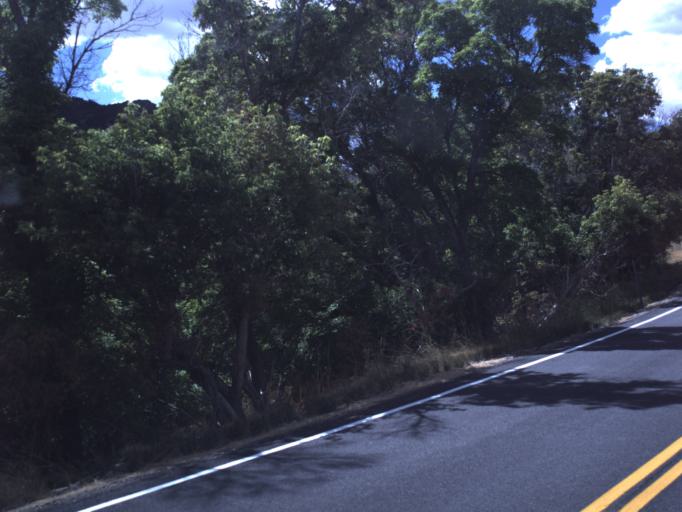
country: US
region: Utah
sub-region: Tooele County
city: Grantsville
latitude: 40.3442
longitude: -112.5456
